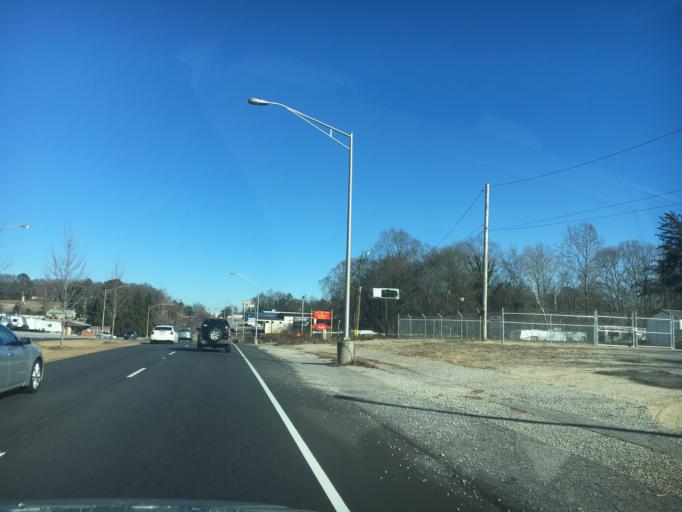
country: US
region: South Carolina
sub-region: Spartanburg County
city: Spartanburg
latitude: 34.9414
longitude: -81.9542
